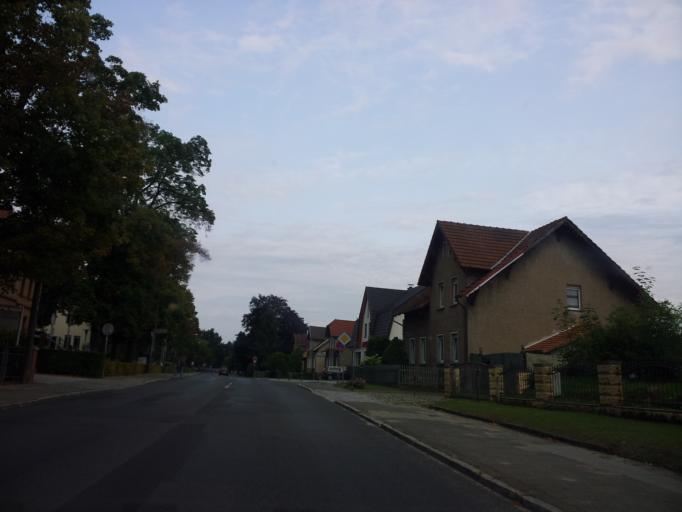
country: DE
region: Brandenburg
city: Belzig
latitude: 52.1402
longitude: 12.5970
